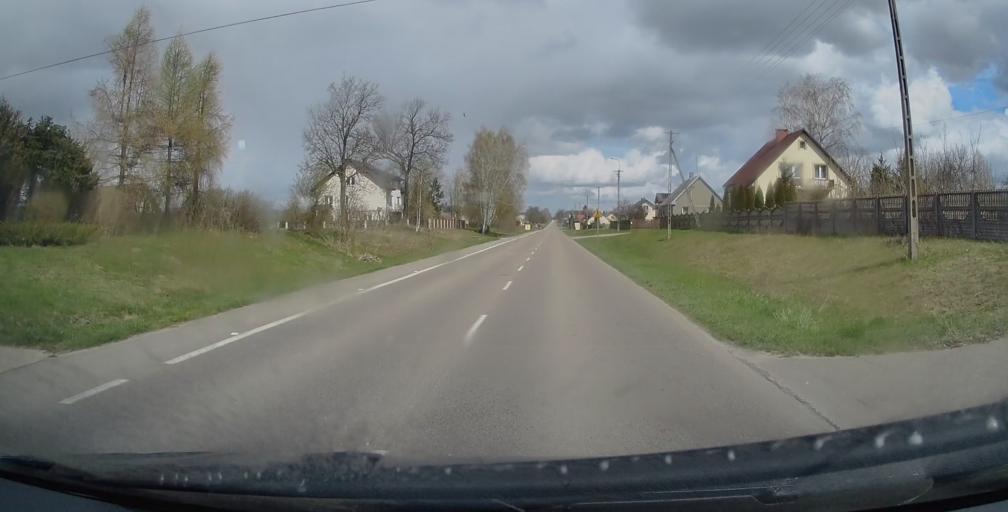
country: PL
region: Masovian Voivodeship
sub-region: Powiat ostrolecki
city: Goworowo
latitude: 52.9526
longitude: 21.5939
